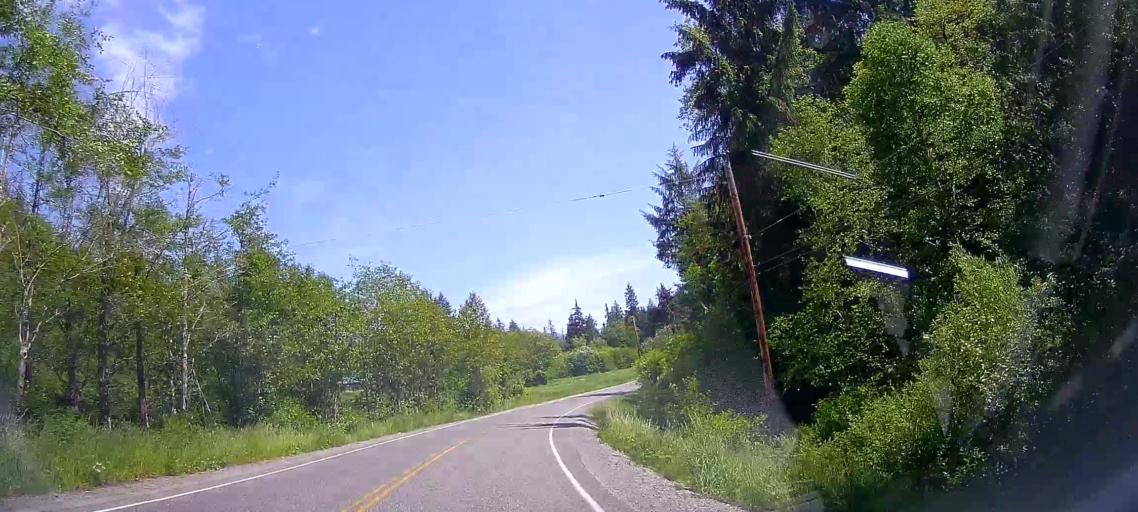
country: US
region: Washington
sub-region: Skagit County
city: Big Lake
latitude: 48.3912
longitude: -122.2578
